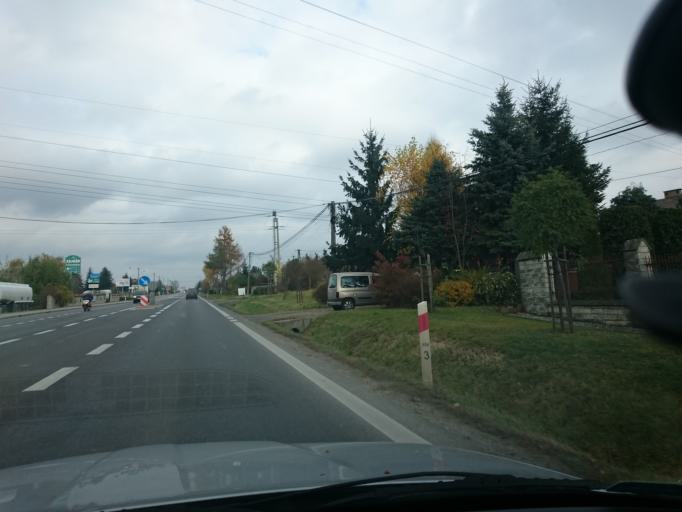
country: PL
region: Lesser Poland Voivodeship
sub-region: Powiat krakowski
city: Michalowice
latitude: 50.1235
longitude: 19.9677
